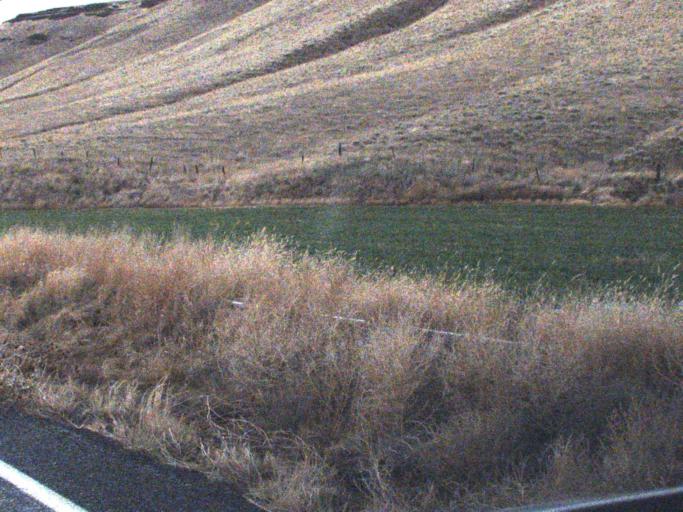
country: US
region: Washington
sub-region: Columbia County
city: Dayton
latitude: 46.5095
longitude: -117.9924
